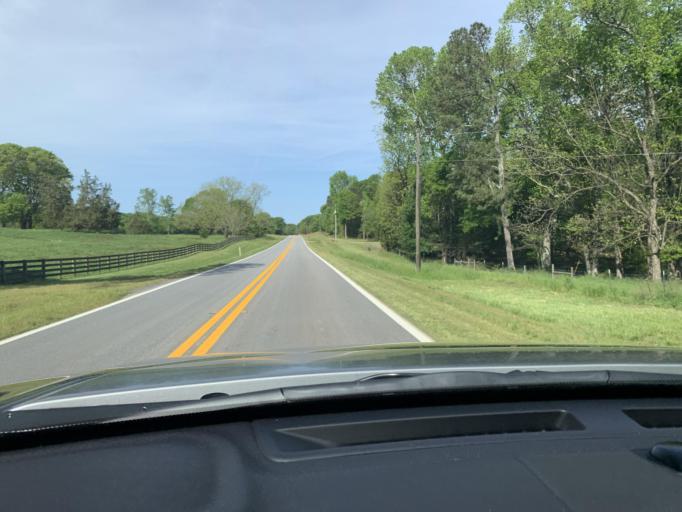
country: US
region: Georgia
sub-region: Oconee County
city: Watkinsville
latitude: 33.8160
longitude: -83.3873
